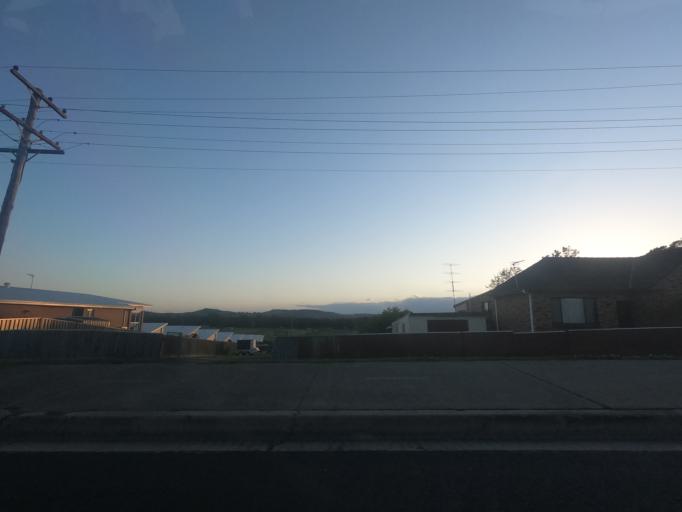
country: AU
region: New South Wales
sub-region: Wollongong
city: Koonawarra
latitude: -34.4991
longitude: 150.8221
